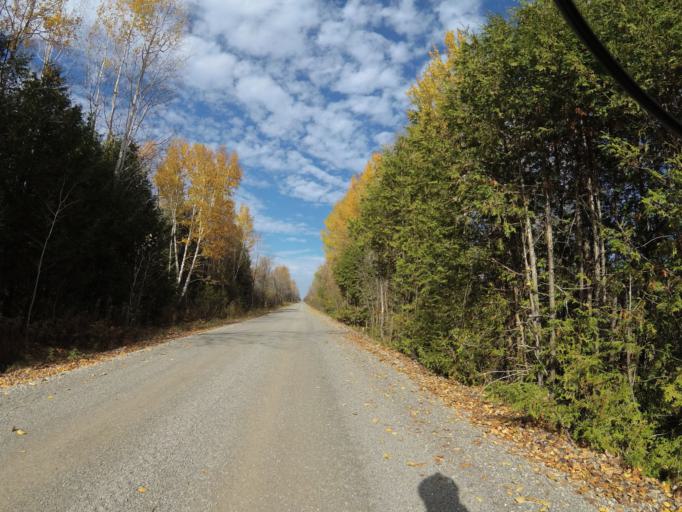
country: CA
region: Ontario
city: Carleton Place
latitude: 45.0329
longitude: -76.0809
